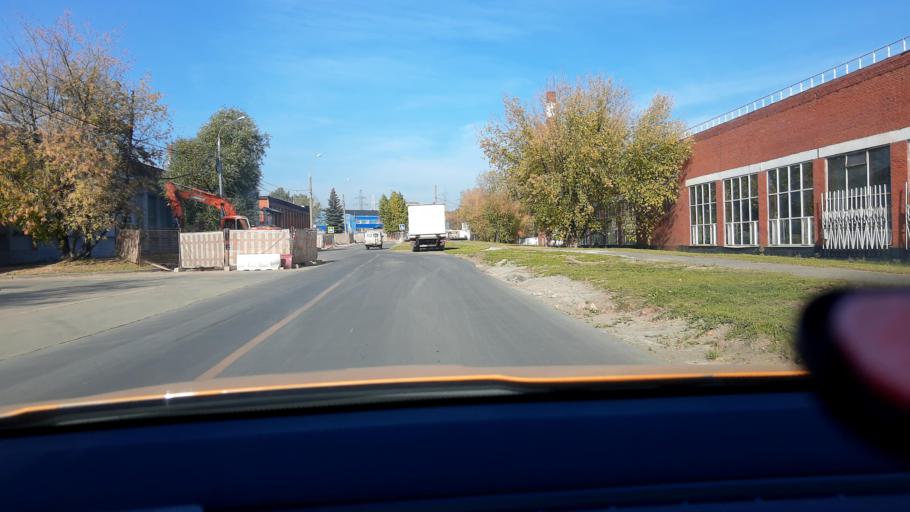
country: RU
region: Moscow
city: Tsaritsyno
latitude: 55.6430
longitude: 37.6423
